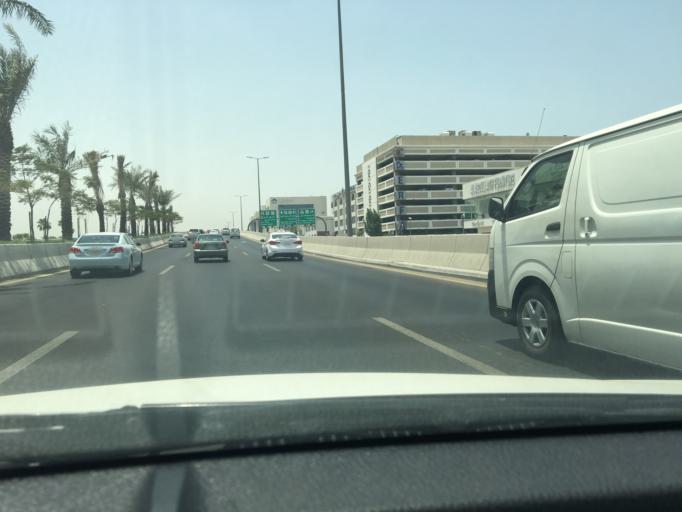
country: SA
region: Makkah
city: Jeddah
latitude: 21.5787
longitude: 39.1788
